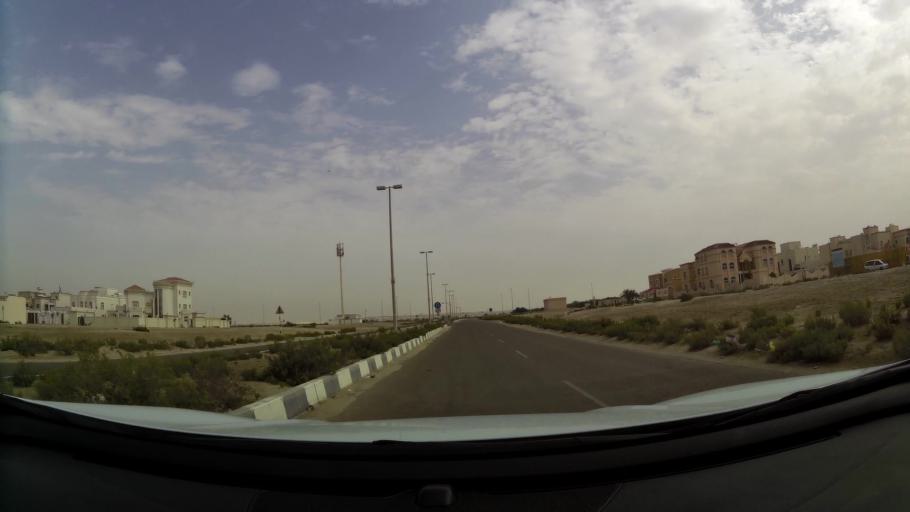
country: AE
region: Abu Dhabi
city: Abu Dhabi
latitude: 24.3088
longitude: 54.6565
